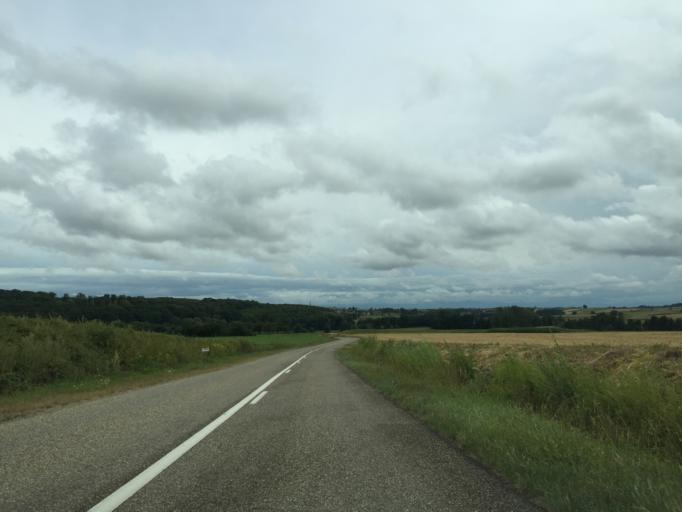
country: FR
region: Alsace
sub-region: Departement du Bas-Rhin
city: Soultz-sous-Forets
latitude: 48.9649
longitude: 7.8877
